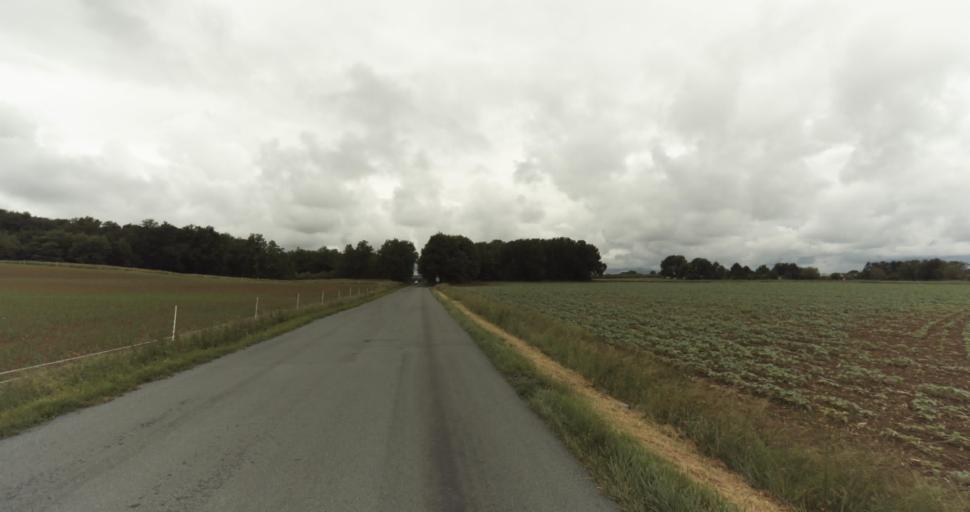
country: FR
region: Aquitaine
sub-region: Departement de la Dordogne
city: Beaumont-du-Perigord
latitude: 44.7079
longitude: 0.8257
